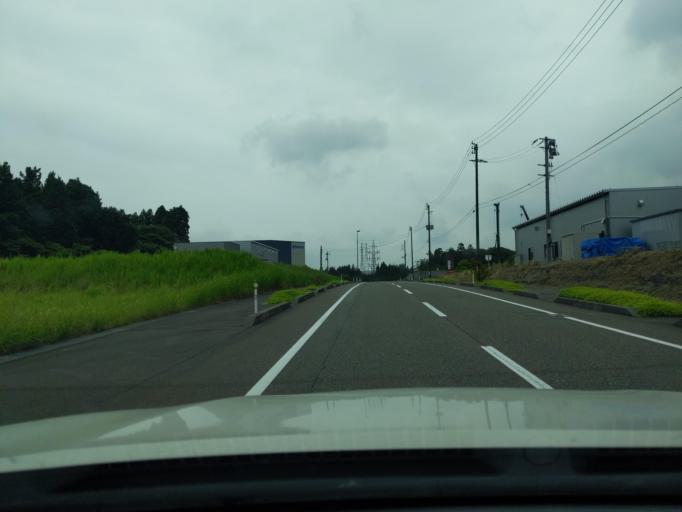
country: JP
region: Niigata
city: Kashiwazaki
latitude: 37.3395
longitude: 138.5900
